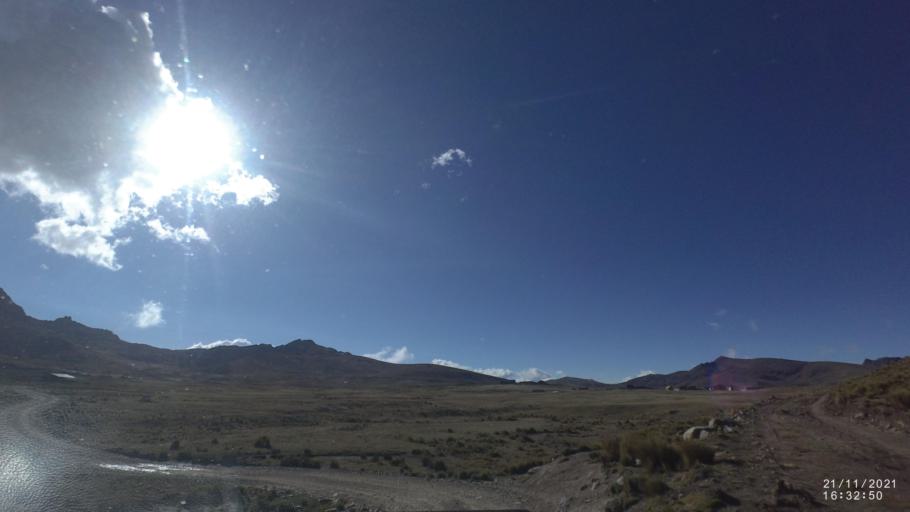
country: BO
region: Cochabamba
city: Cochabamba
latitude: -17.0316
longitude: -66.2769
